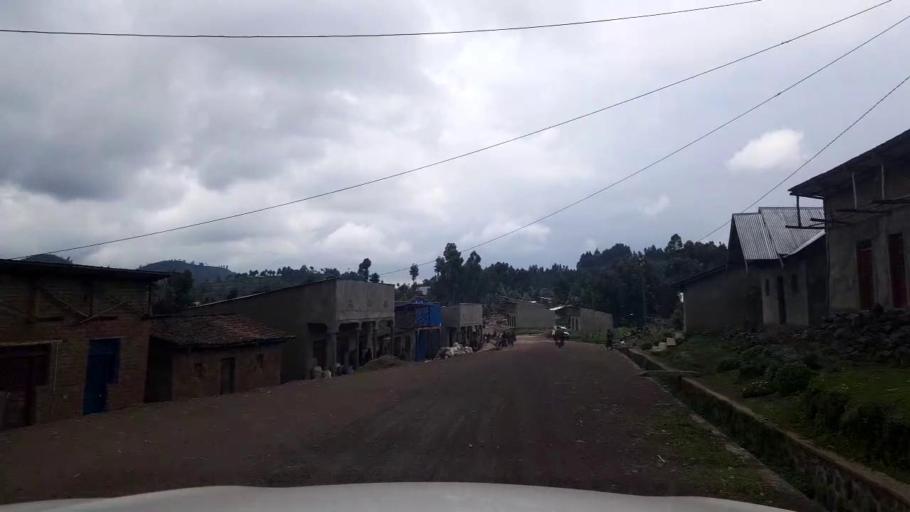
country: RW
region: Northern Province
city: Musanze
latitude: -1.5775
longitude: 29.4872
